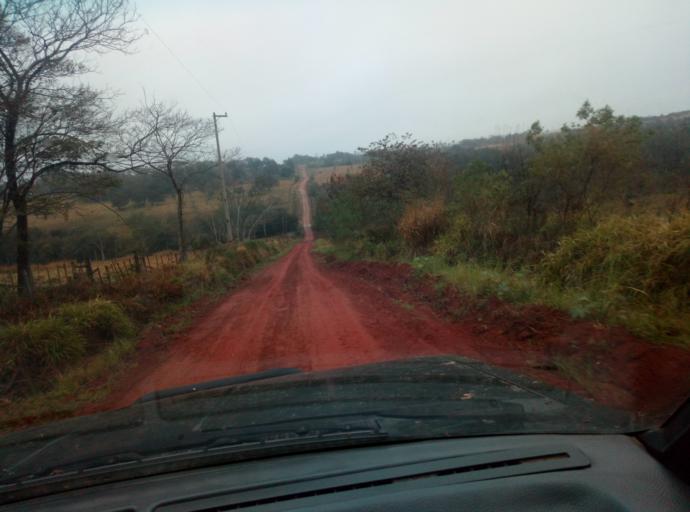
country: PY
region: Caaguazu
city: Carayao
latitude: -25.1904
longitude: -56.3131
